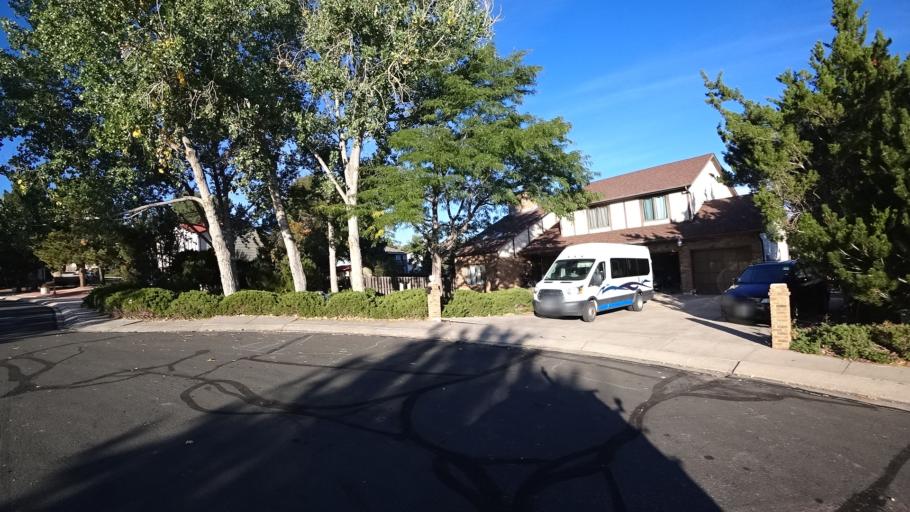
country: US
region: Colorado
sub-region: El Paso County
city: Cimarron Hills
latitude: 38.8881
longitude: -104.7645
